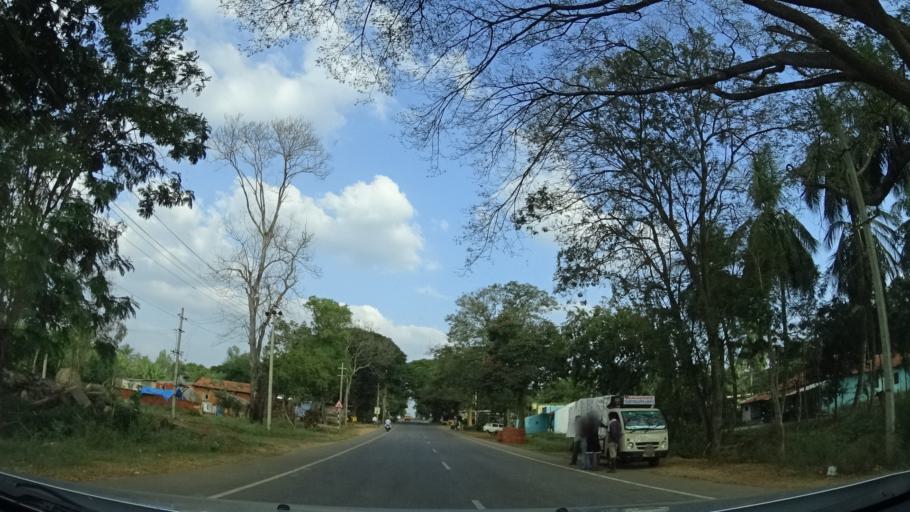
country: IN
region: Karnataka
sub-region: Mandya
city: Malavalli
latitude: 12.3691
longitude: 77.0099
